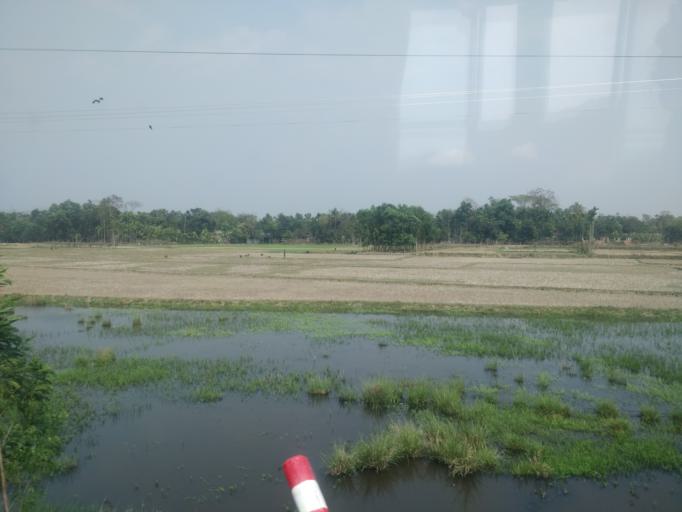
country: BD
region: Sylhet
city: Habiganj
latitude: 24.3228
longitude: 91.4340
